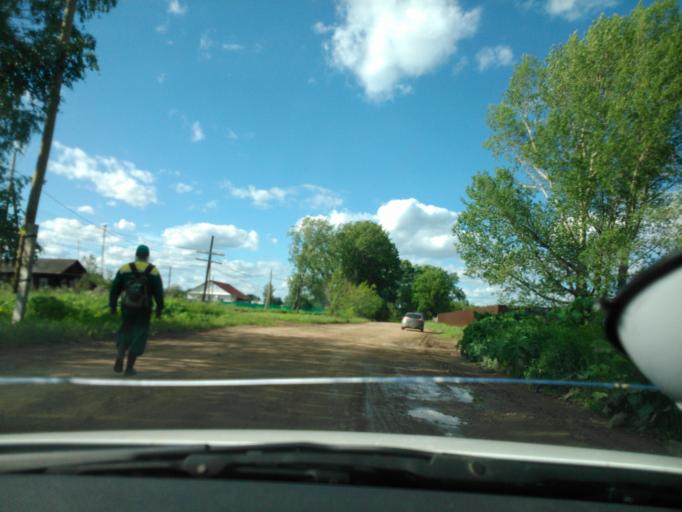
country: RU
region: Perm
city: Ust'-Kachka
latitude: 57.9435
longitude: 55.7440
